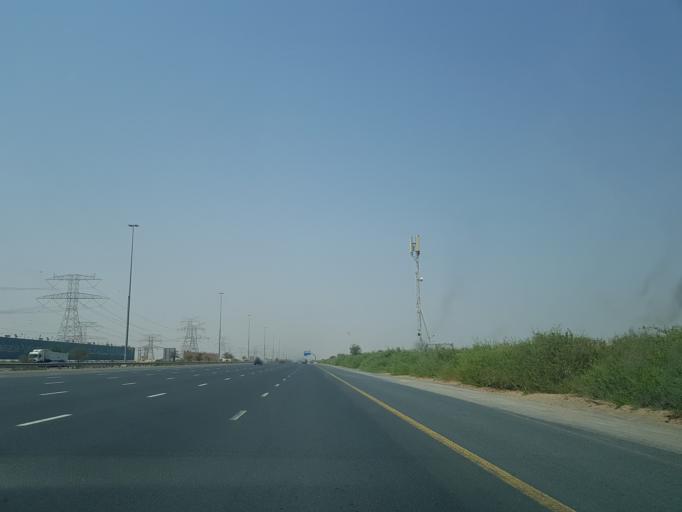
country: AE
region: Ash Shariqah
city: Sharjah
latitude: 25.1206
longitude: 55.4402
